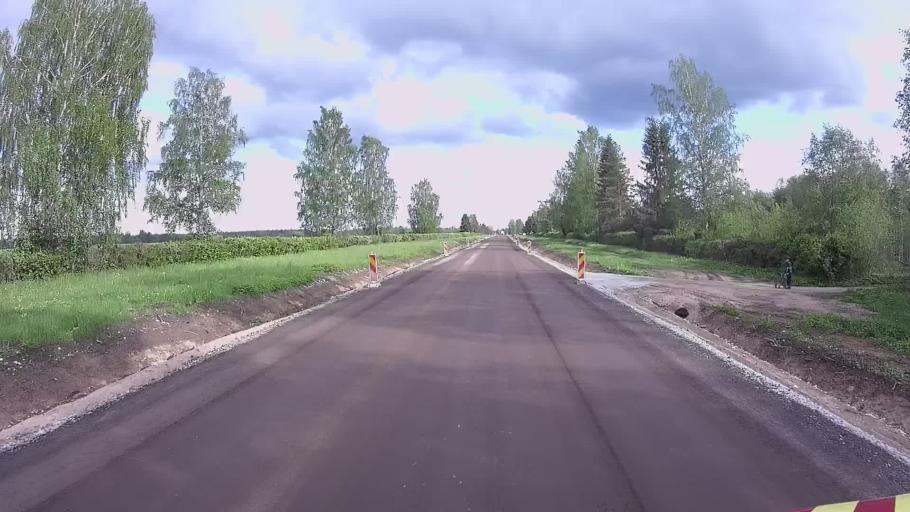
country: EE
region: Jogevamaa
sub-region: Mustvee linn
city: Mustvee
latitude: 59.0243
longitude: 26.6976
